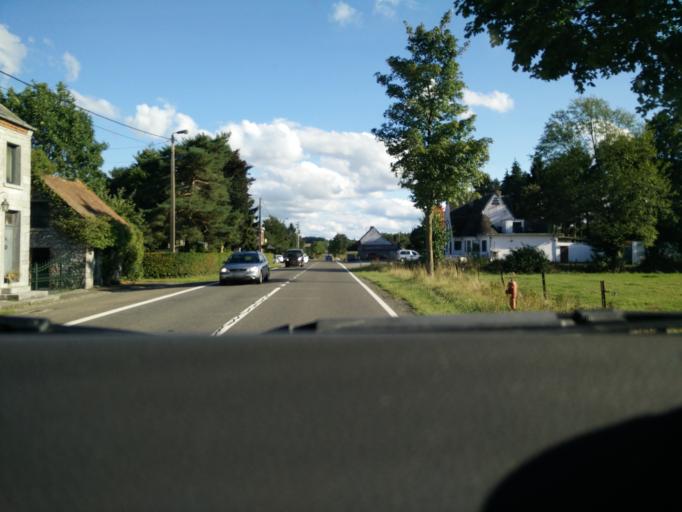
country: BE
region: Wallonia
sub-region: Province du Hainaut
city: Beaumont
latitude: 50.2624
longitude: 4.2192
